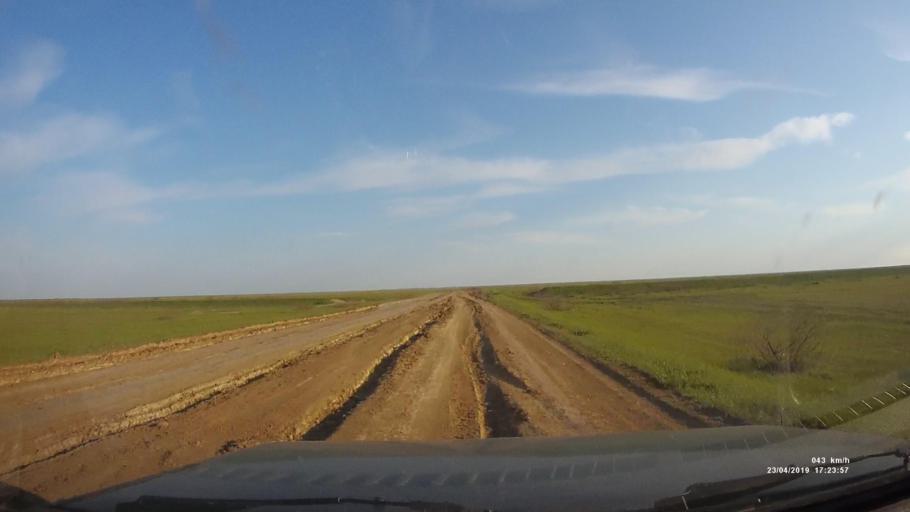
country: RU
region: Kalmykiya
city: Priyutnoye
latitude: 46.1593
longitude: 43.5081
